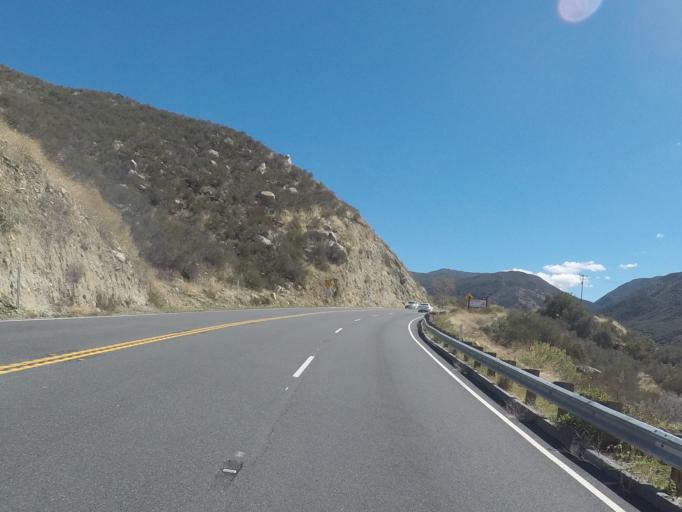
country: US
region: California
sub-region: Riverside County
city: Idyllwild-Pine Cove
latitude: 33.7209
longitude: -116.7952
